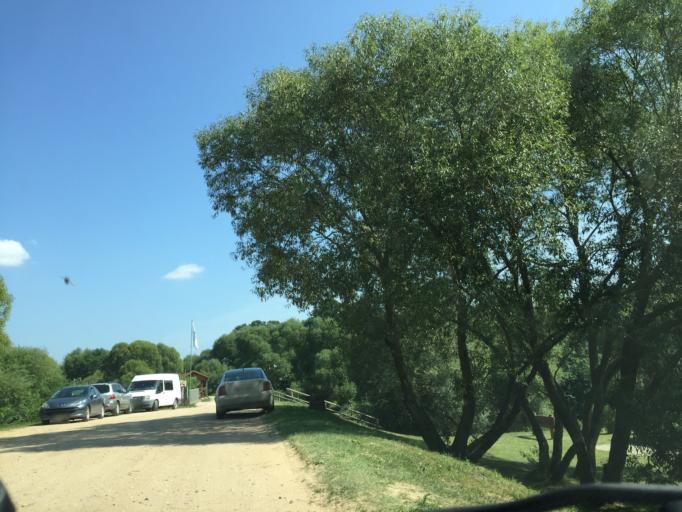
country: LV
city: Tervete
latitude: 56.4969
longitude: 23.4105
